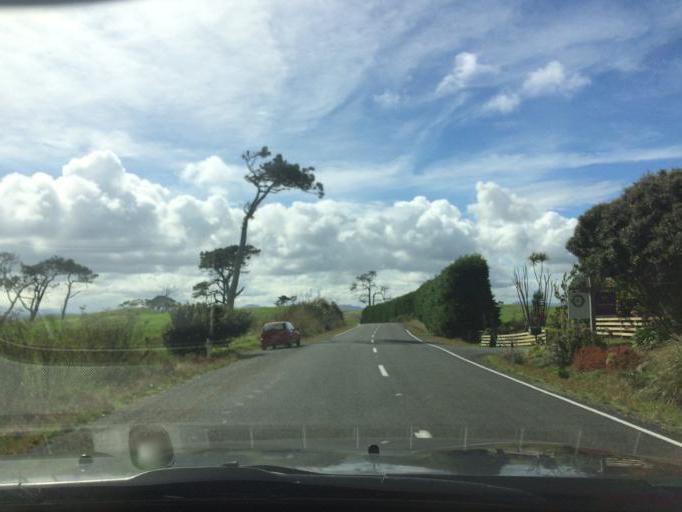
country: NZ
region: Northland
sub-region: Kaipara District
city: Dargaville
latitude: -35.9476
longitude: 173.7697
